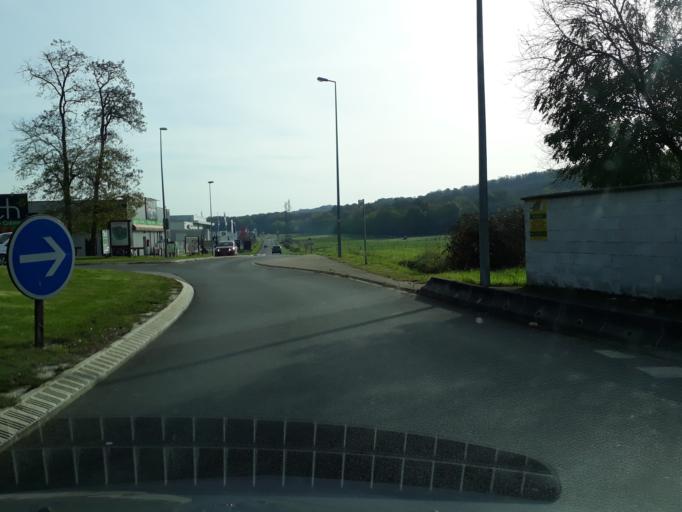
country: FR
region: Ile-de-France
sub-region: Departement de Seine-et-Marne
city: Samoreau
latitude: 48.4250
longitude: 2.7617
